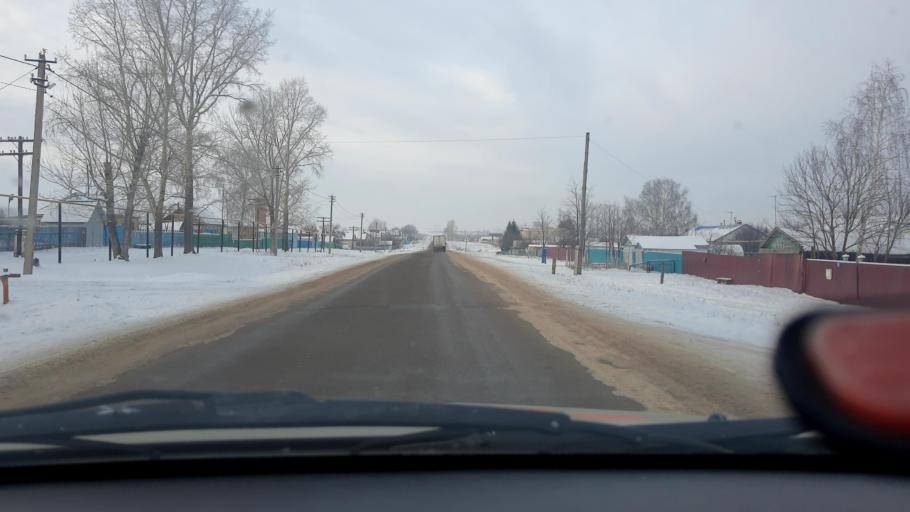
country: RU
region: Bashkortostan
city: Avdon
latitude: 54.3607
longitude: 55.8398
